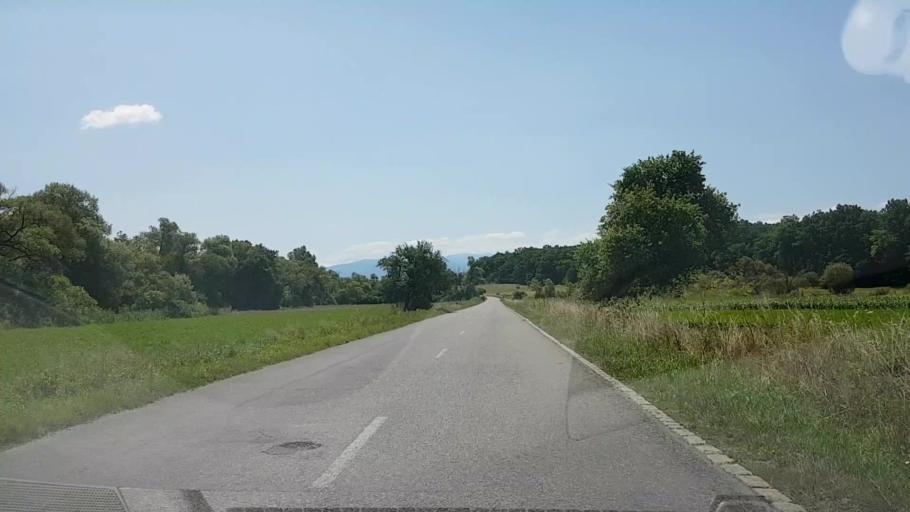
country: RO
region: Brasov
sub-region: Comuna Cincu
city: Cincu
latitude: 45.8750
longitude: 24.8192
